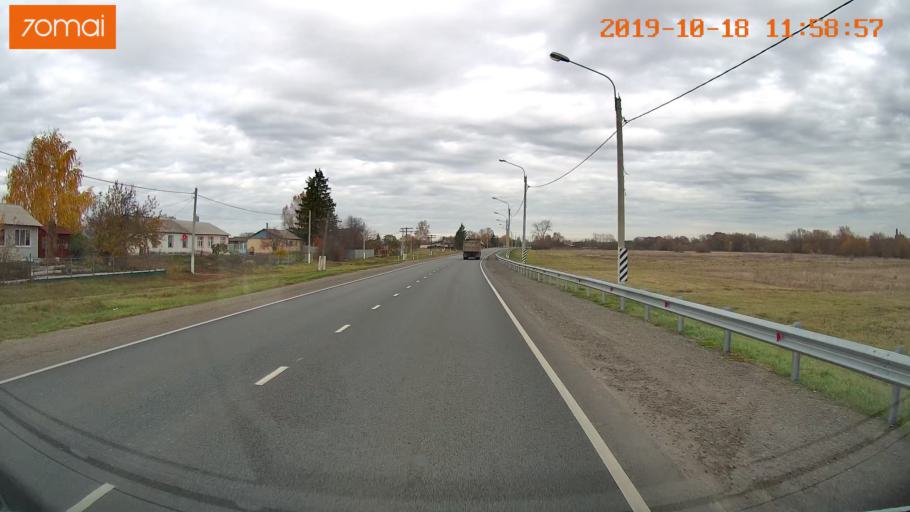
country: RU
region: Rjazan
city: Zakharovo
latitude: 54.2771
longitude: 39.1712
